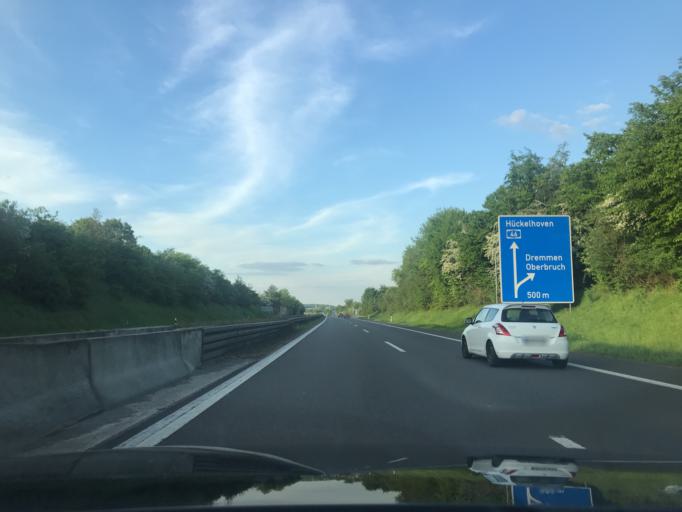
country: DE
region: North Rhine-Westphalia
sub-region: Regierungsbezirk Koln
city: Wassenberg
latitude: 51.0381
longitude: 6.1566
